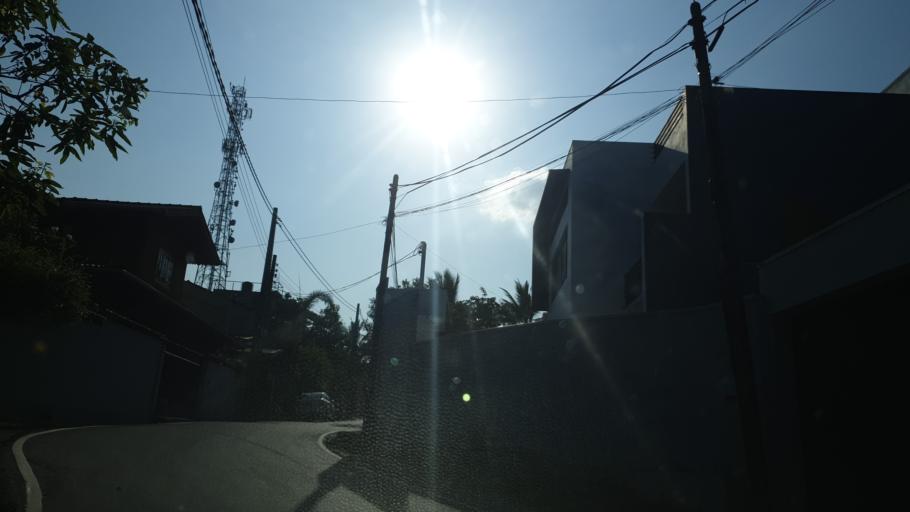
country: LK
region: Western
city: Battaramulla South
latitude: 6.8867
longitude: 79.9434
